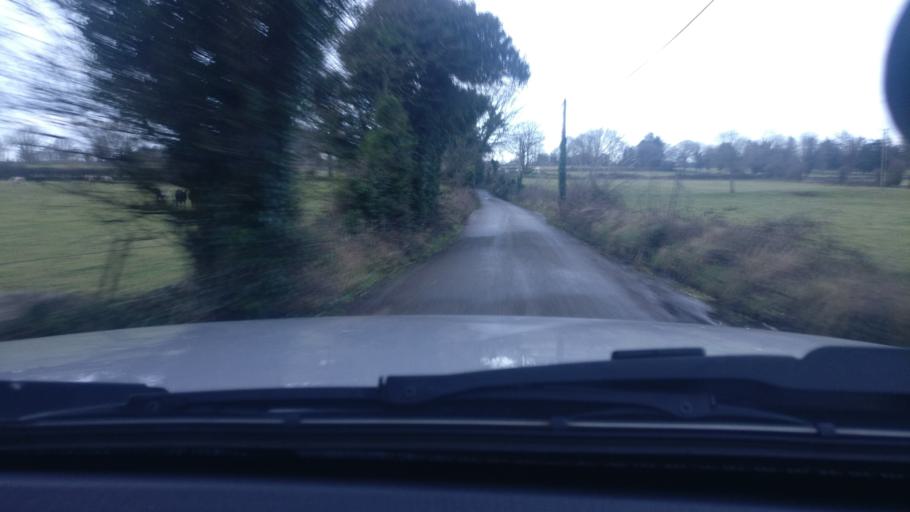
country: IE
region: Connaught
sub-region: County Galway
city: Loughrea
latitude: 53.1770
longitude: -8.5086
